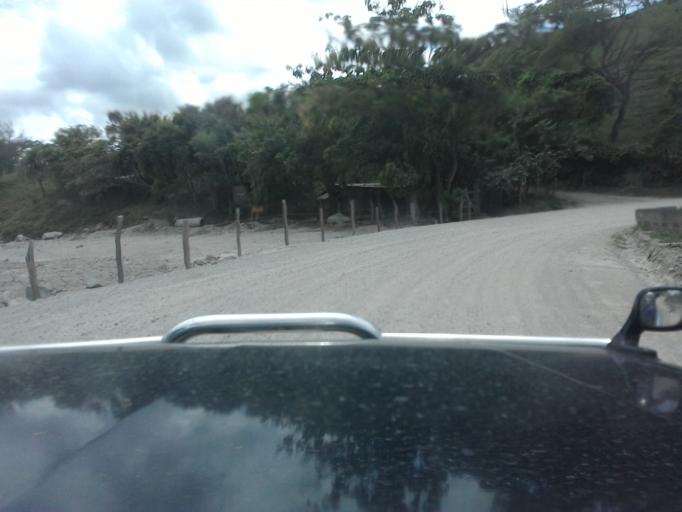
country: CR
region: Guanacaste
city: Juntas
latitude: 10.2388
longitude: -84.8536
